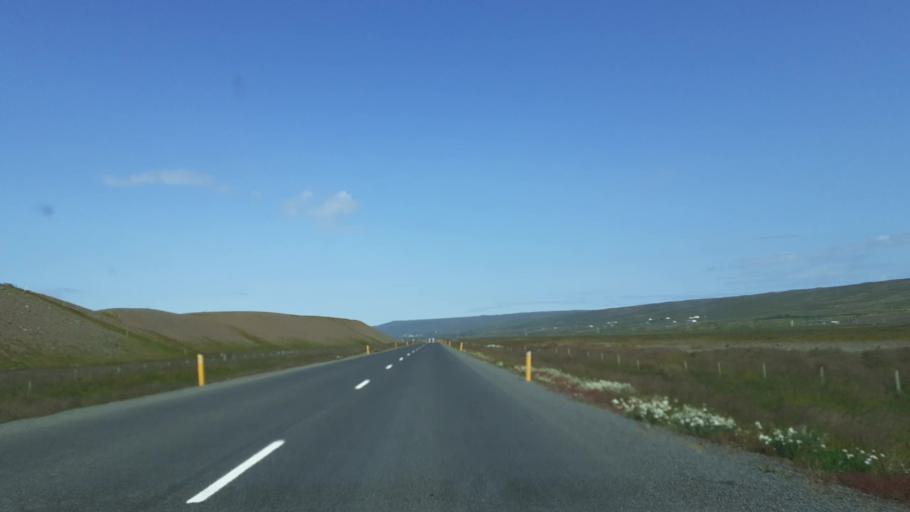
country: IS
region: West
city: Borgarnes
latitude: 65.1214
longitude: -21.0909
